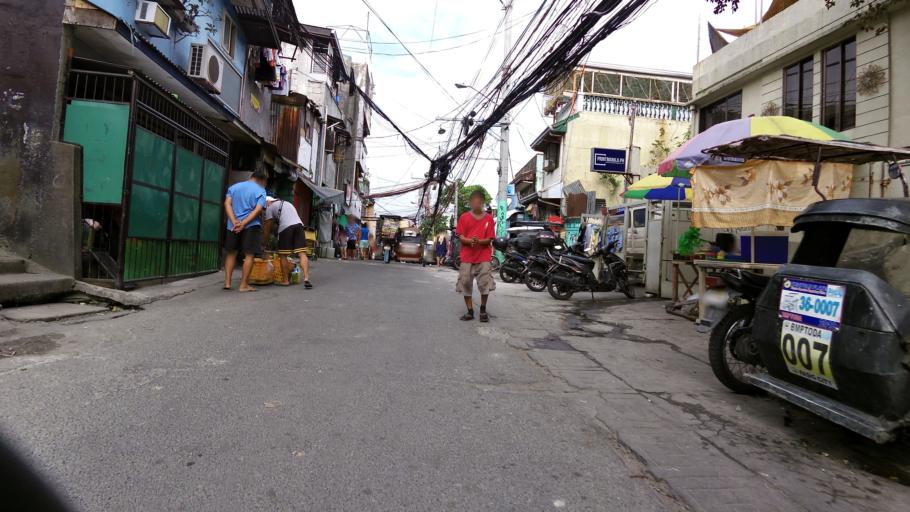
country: PH
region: Metro Manila
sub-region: Pasig
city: Pasig City
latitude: 14.5666
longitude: 121.0570
